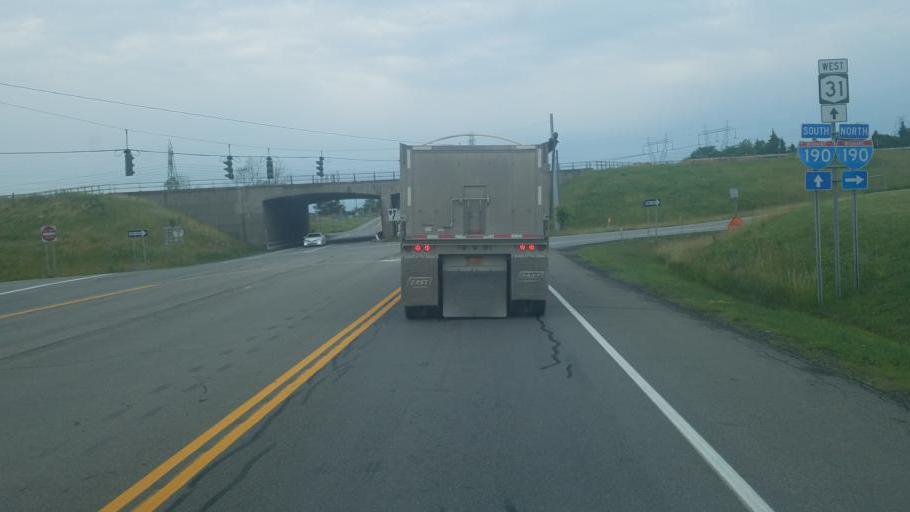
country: US
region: New York
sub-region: Niagara County
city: Lewiston
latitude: 43.1302
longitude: -79.0173
